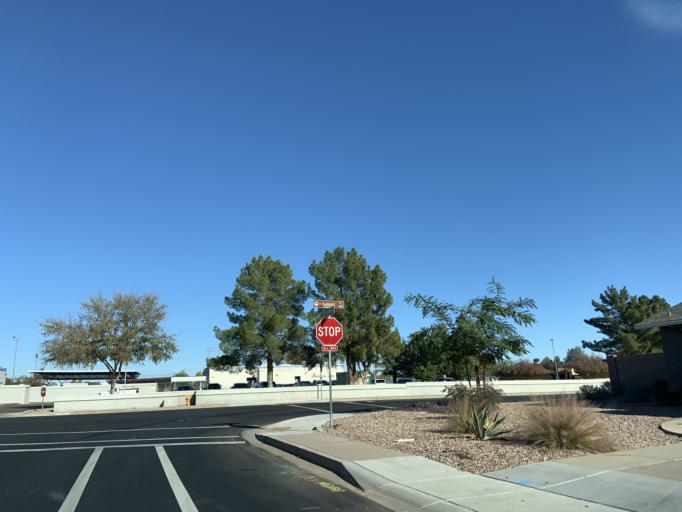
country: US
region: Arizona
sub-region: Maricopa County
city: San Carlos
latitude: 33.3539
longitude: -111.8685
